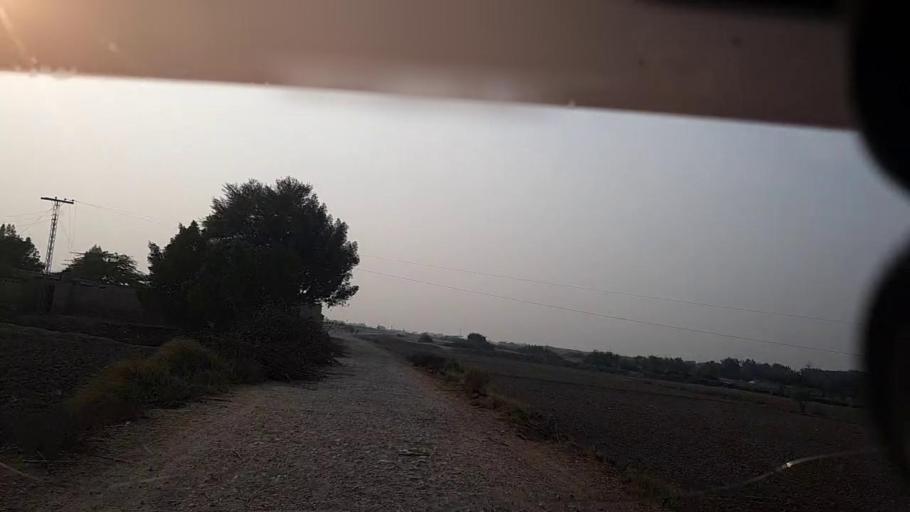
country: PK
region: Sindh
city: Gambat
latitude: 27.4360
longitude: 68.6175
